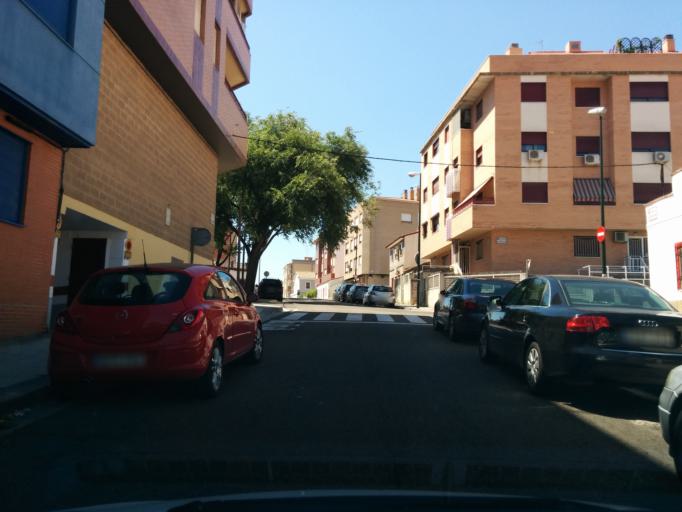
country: ES
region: Aragon
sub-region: Provincia de Zaragoza
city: Zaragoza
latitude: 41.6262
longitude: -0.8761
